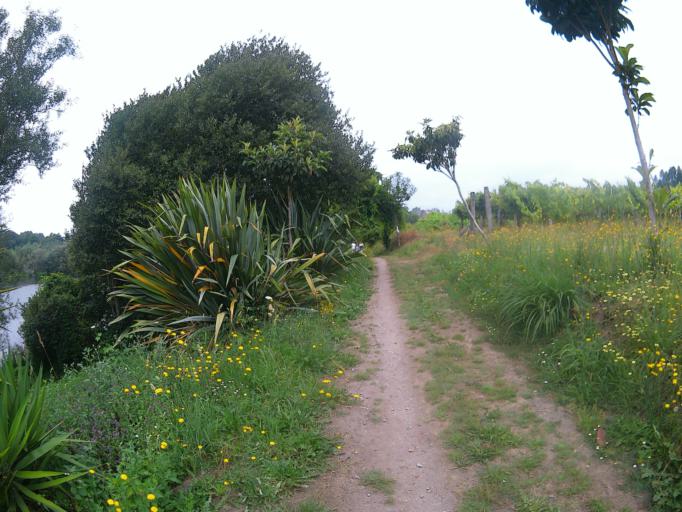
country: PT
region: Viana do Castelo
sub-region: Ponte de Lima
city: Ponte de Lima
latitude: 41.7765
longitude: -8.5636
